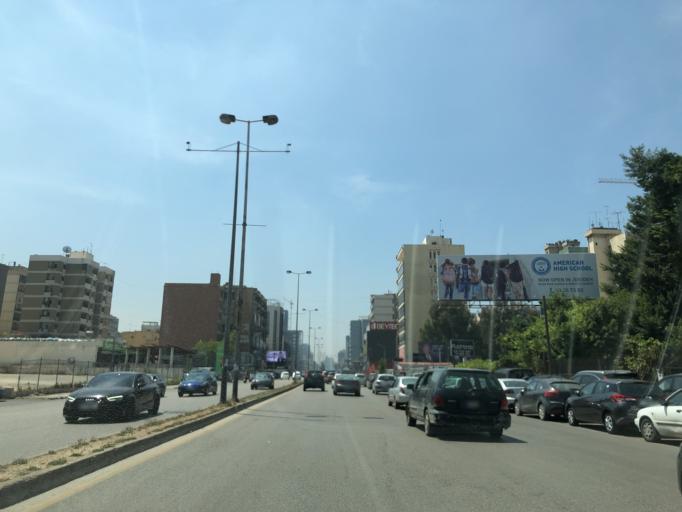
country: LB
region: Mont-Liban
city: Jdaidet el Matn
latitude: 33.8911
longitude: 35.5567
